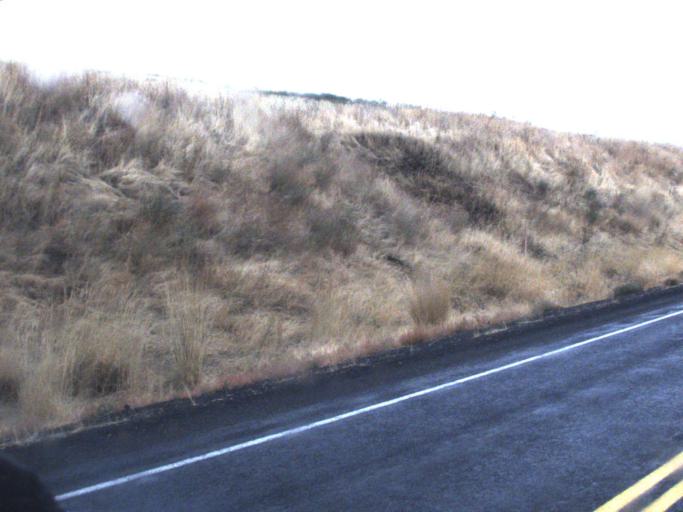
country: US
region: Washington
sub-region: Spokane County
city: Cheney
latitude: 47.1115
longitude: -117.7094
